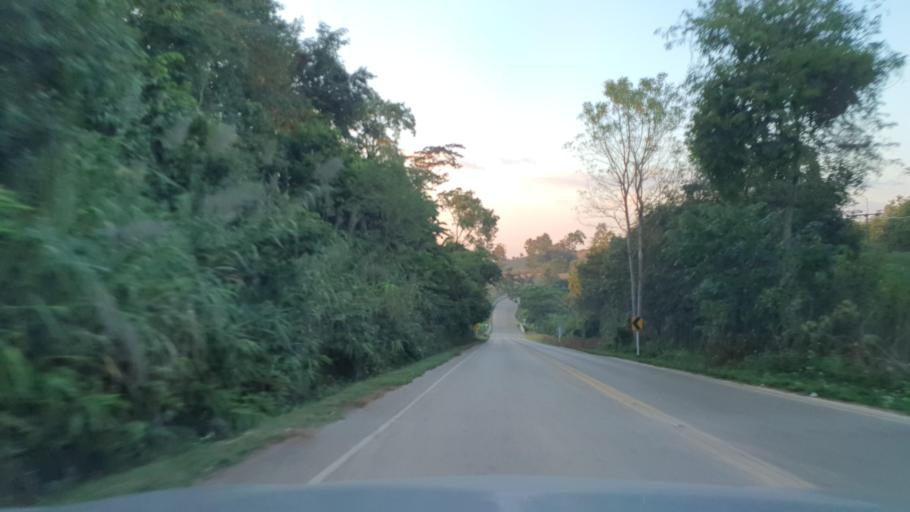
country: TH
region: Lampang
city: Ngao
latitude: 18.9393
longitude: 100.0784
